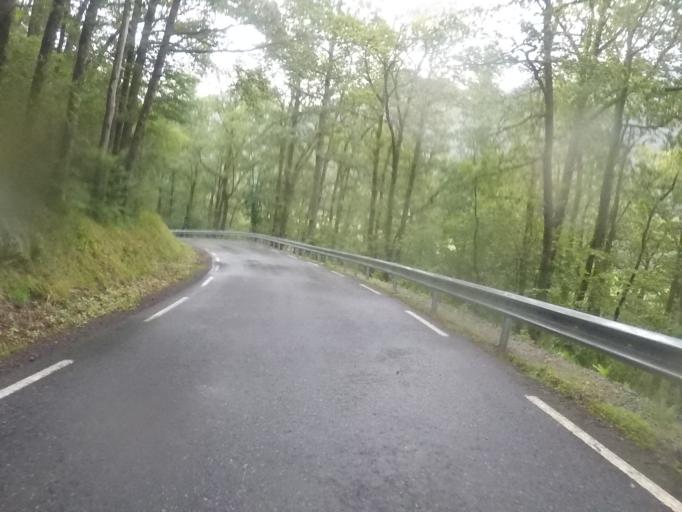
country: NO
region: Vest-Agder
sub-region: Lyngdal
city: Lyngdal
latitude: 58.2355
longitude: 7.1611
